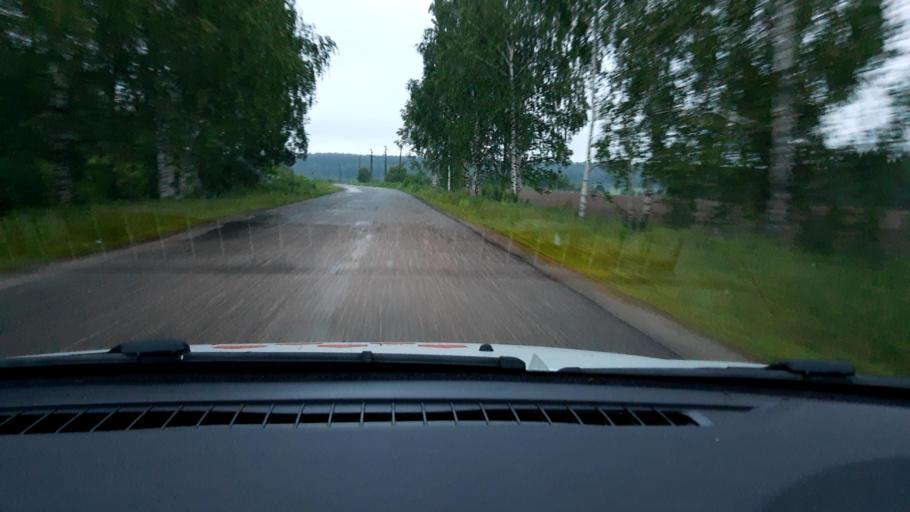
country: RU
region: Nizjnij Novgorod
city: Novaya Balakhna
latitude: 56.6343
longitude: 43.6252
